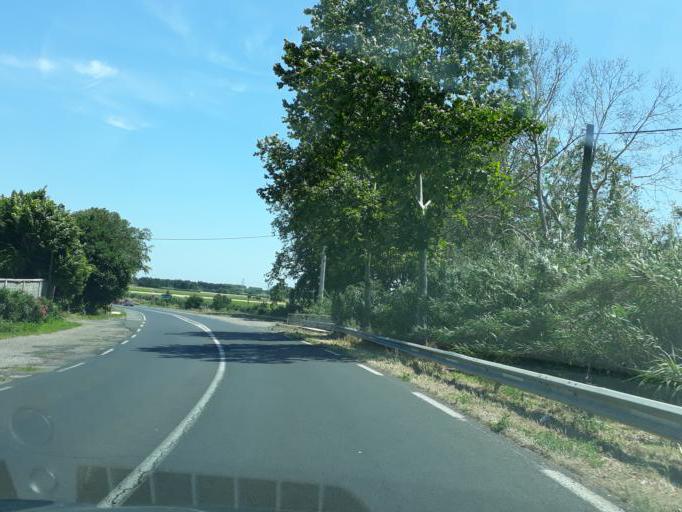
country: FR
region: Languedoc-Roussillon
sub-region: Departement de l'Herault
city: Sauvian
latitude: 43.3242
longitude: 3.2472
